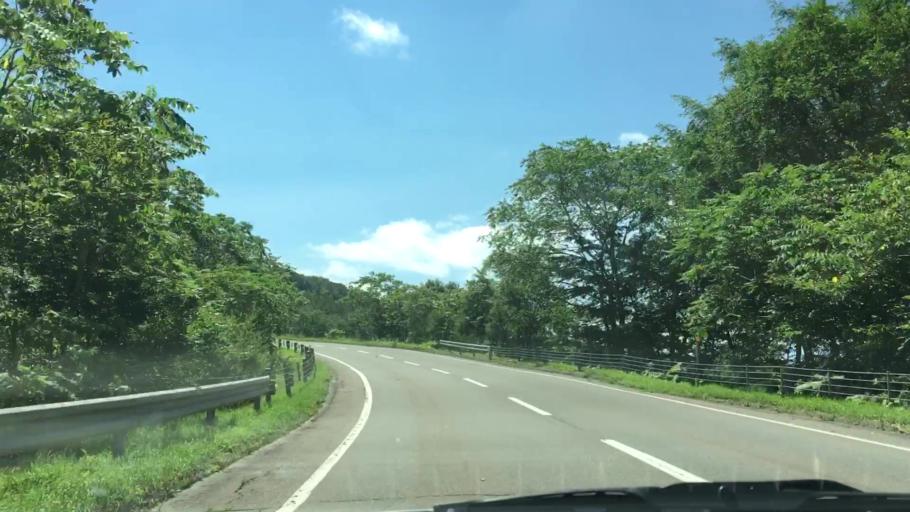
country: JP
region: Hokkaido
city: Kitami
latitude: 43.3197
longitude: 143.7225
